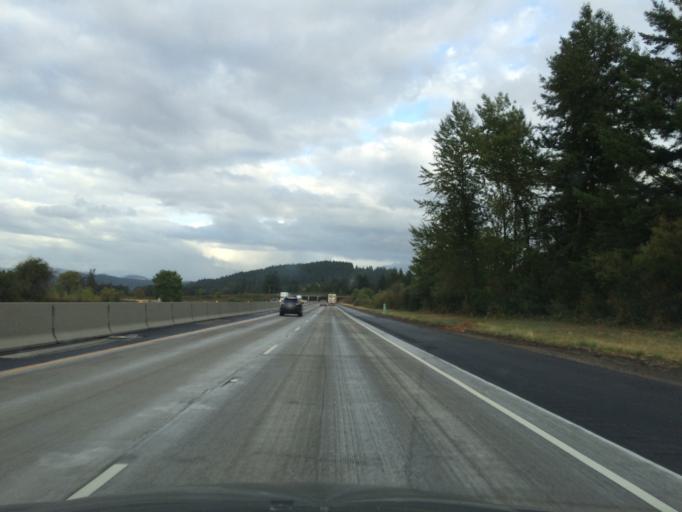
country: US
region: Oregon
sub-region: Lane County
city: Cottage Grove
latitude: 43.7498
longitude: -123.1200
